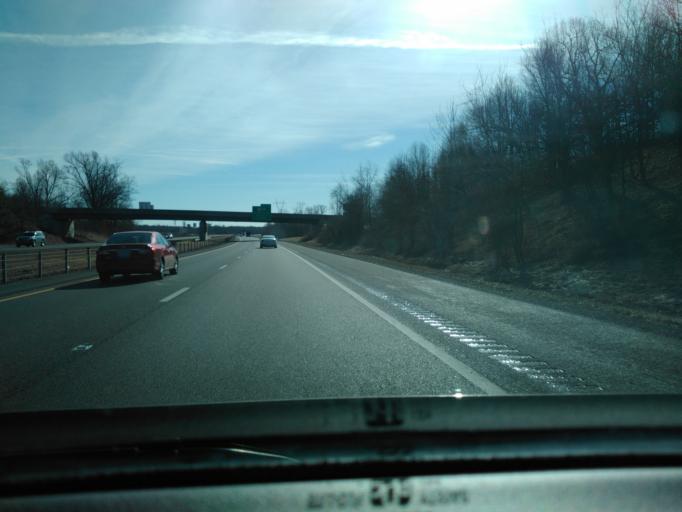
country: US
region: Kentucky
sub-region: McCracken County
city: Hendron
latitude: 37.0359
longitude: -88.6293
